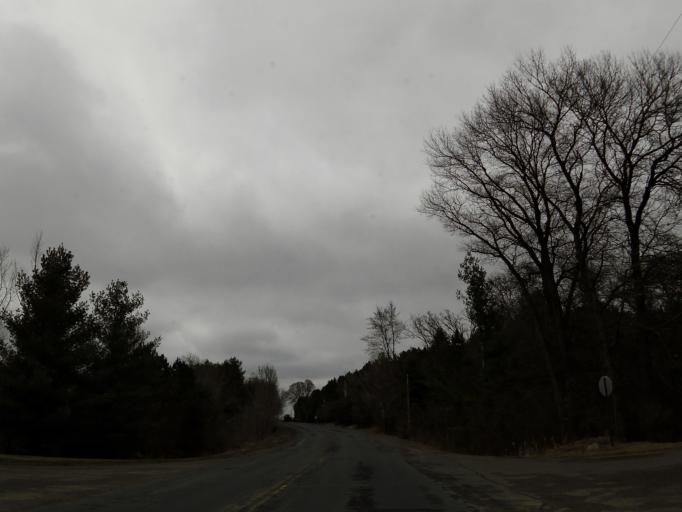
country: US
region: Minnesota
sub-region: Washington County
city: Oak Park Heights
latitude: 45.0163
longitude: -92.8281
